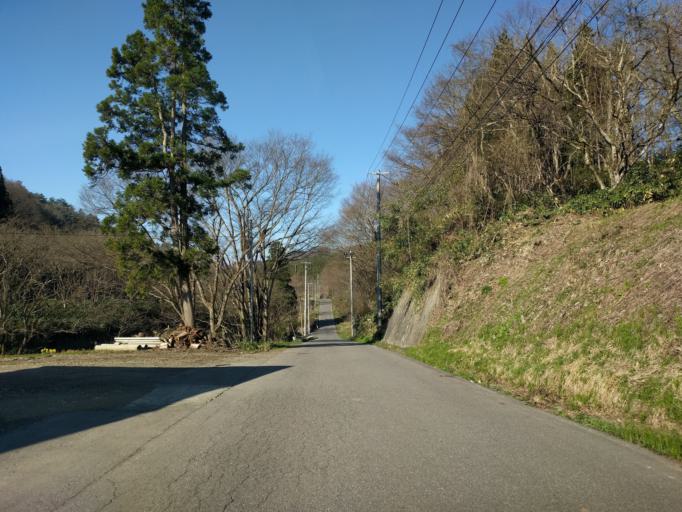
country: JP
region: Fukushima
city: Kitakata
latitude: 37.6669
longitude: 139.8085
